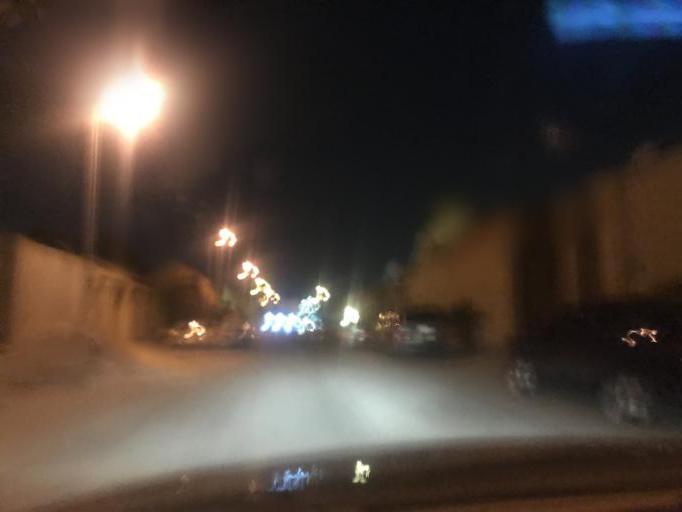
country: SA
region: Ar Riyad
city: Riyadh
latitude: 24.7430
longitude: 46.7861
